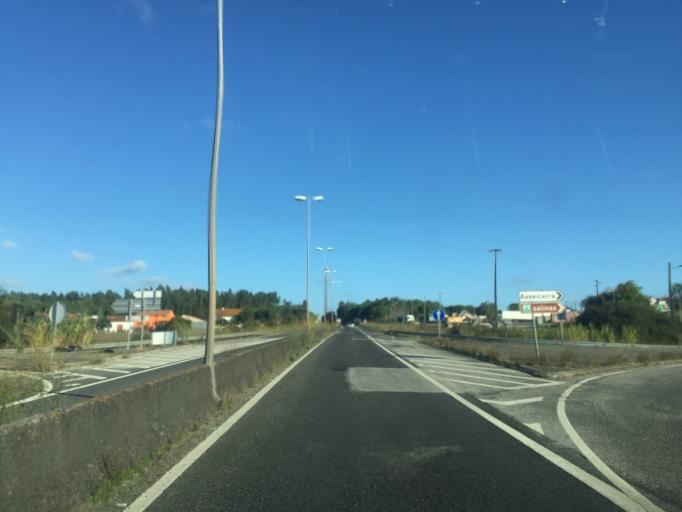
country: PT
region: Santarem
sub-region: Rio Maior
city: Rio Maior
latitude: 39.2820
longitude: -8.9415
